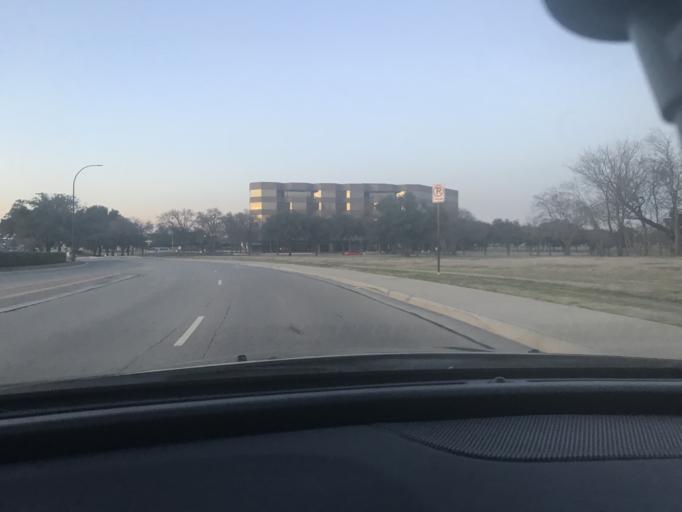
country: US
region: Texas
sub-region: Tarrant County
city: Arlington
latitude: 32.7621
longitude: -97.1016
